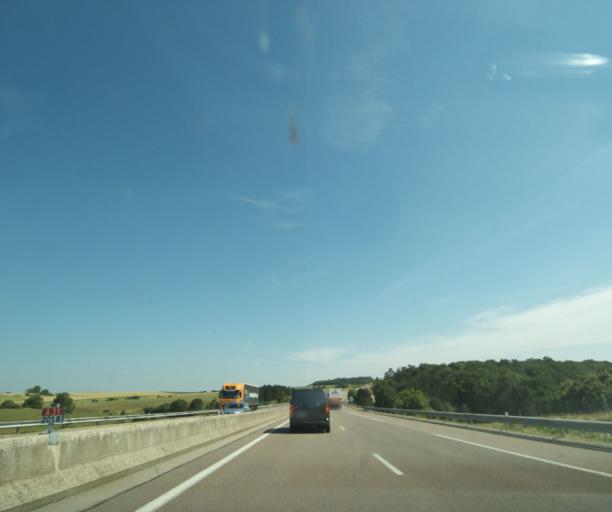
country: FR
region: Lorraine
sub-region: Departement de Meurthe-et-Moselle
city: Colombey-les-Belles
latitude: 48.4311
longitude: 5.8601
